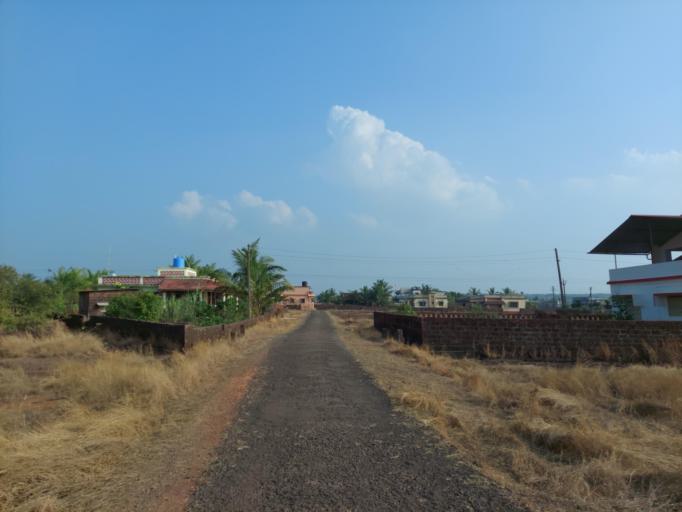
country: IN
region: Maharashtra
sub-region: Ratnagiri
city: Ratnagiri
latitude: 16.9348
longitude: 73.3253
